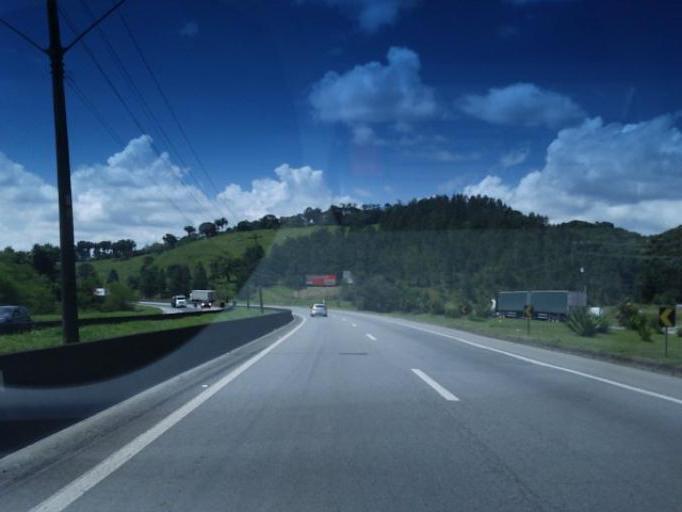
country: BR
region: Sao Paulo
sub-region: Sao Lourenco Da Serra
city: Sao Lourenco da Serra
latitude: -23.9100
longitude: -46.9917
